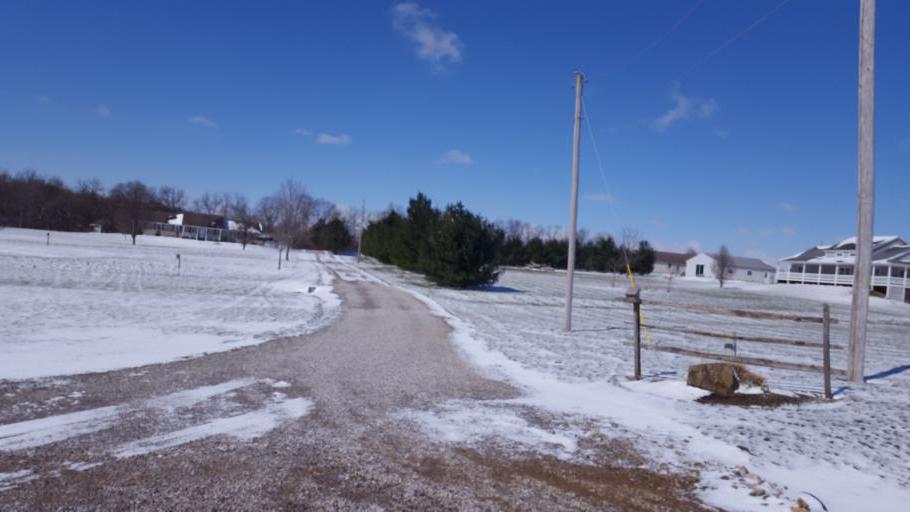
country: US
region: Ohio
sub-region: Knox County
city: Fredericktown
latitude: 40.4729
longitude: -82.6008
